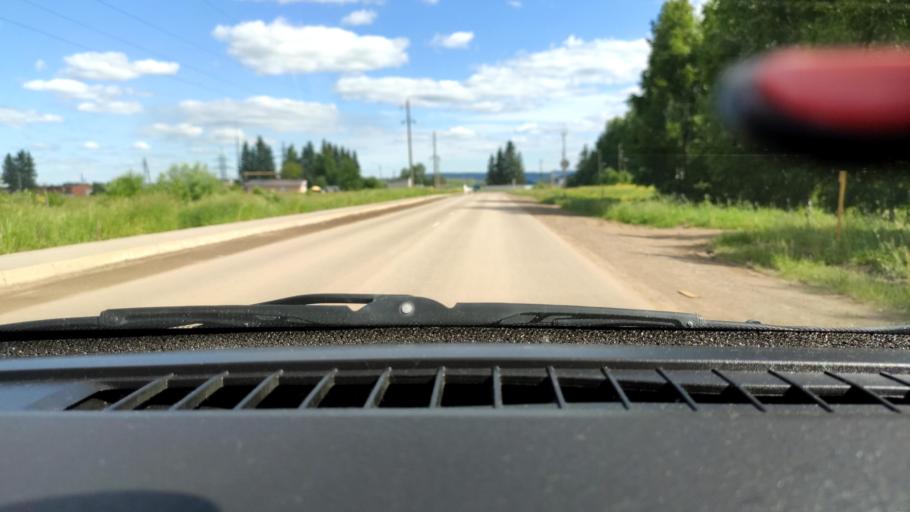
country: RU
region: Perm
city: Kultayevo
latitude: 57.8894
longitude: 55.9220
